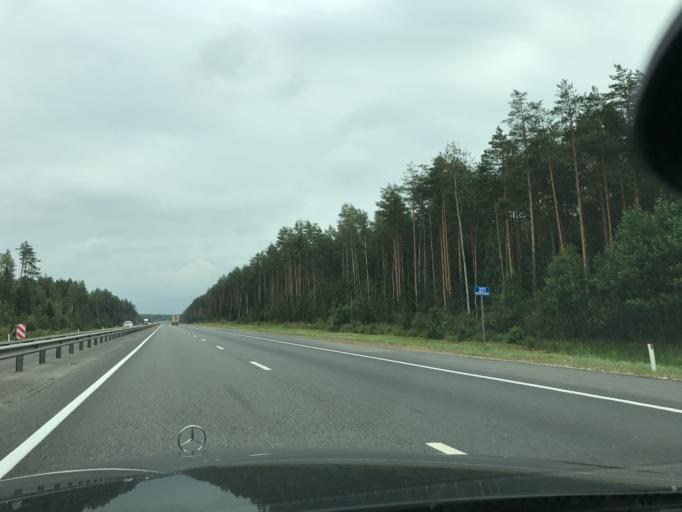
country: RU
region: Vladimir
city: Kameshkovo
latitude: 56.1794
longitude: 40.9468
